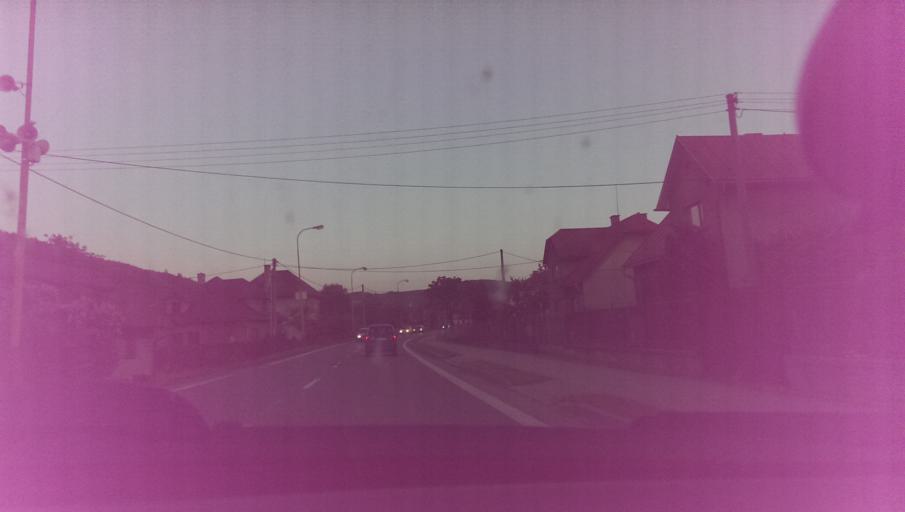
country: CZ
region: Zlin
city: Valasska Polanka
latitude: 49.2658
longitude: 17.9962
